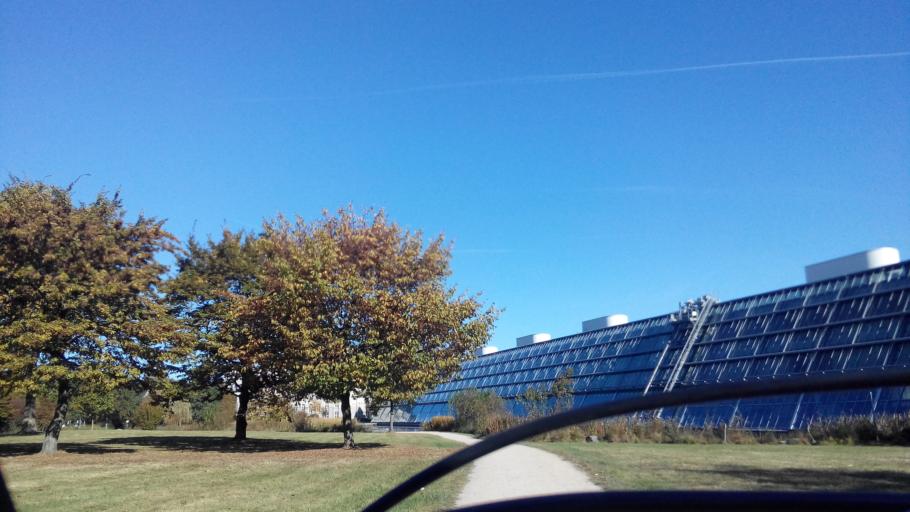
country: DE
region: North Rhine-Westphalia
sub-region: Regierungsbezirk Munster
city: Gelsenkirchen
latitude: 51.4984
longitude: 7.1068
